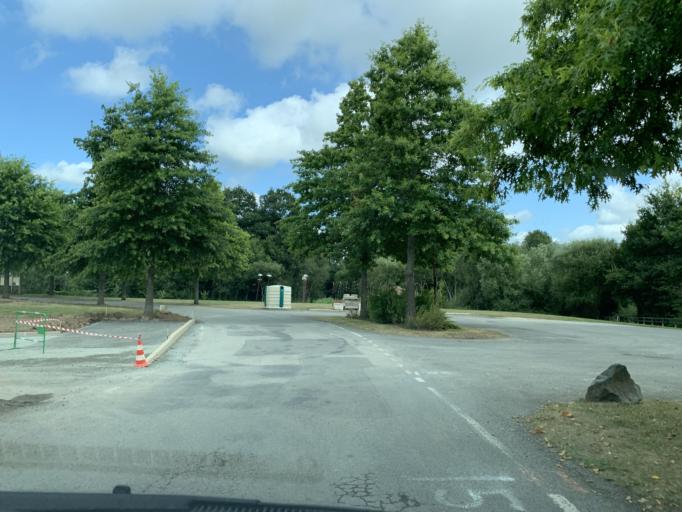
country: FR
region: Brittany
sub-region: Departement du Morbihan
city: Noyal-Muzillac
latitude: 47.5832
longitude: -2.4065
